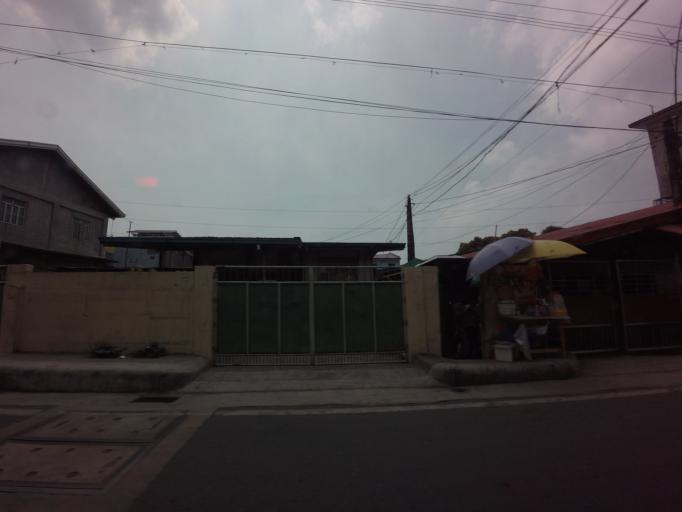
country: PH
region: Calabarzon
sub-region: Province of Rizal
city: Taguig
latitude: 14.4730
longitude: 121.0587
